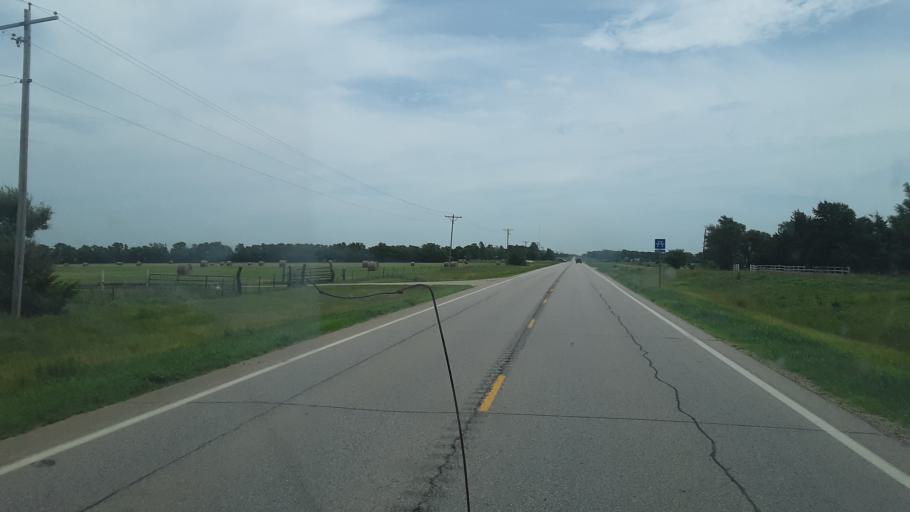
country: US
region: Kansas
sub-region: Butler County
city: El Dorado
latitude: 37.8105
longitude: -96.6660
